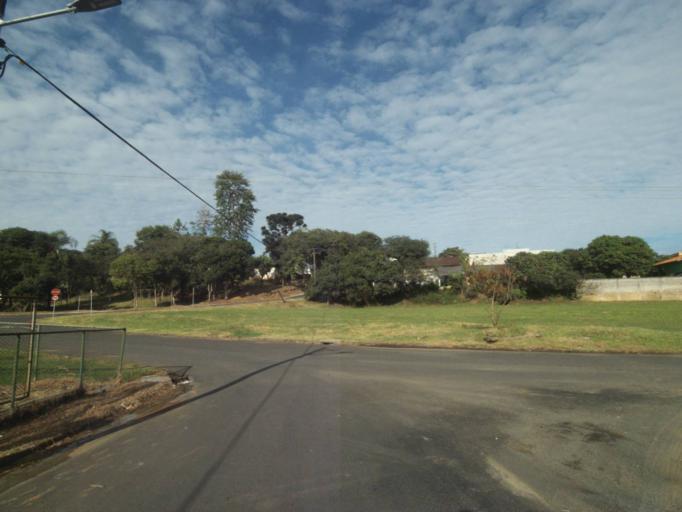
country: BR
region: Parana
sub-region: Telemaco Borba
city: Telemaco Borba
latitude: -24.3438
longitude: -50.6095
